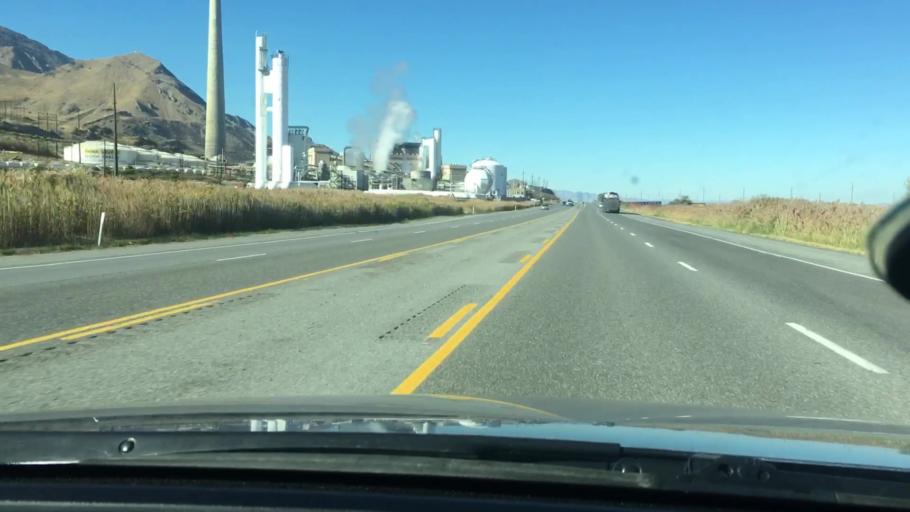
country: US
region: Utah
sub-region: Salt Lake County
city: Magna
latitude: 40.7276
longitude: -112.1816
